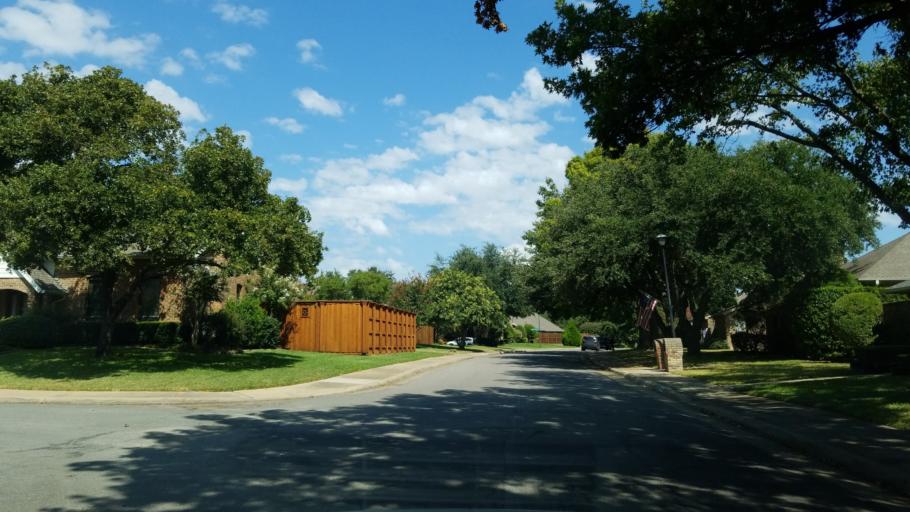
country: US
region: Texas
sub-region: Dallas County
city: Addison
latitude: 32.9571
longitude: -96.7986
